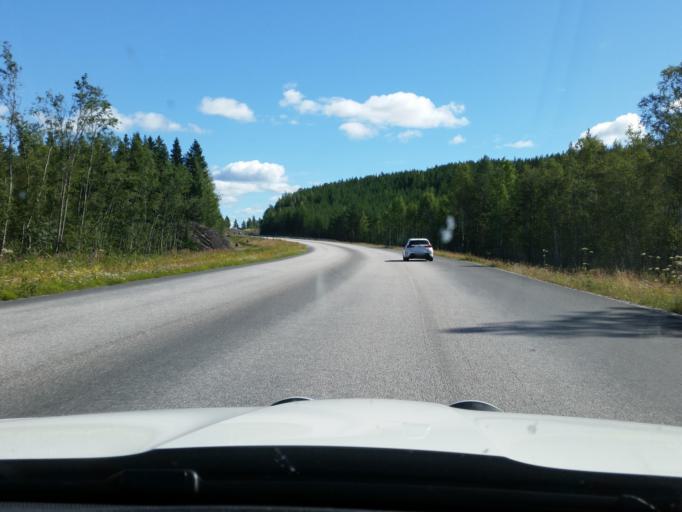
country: SE
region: Norrbotten
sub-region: Pitea Kommun
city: Bergsviken
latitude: 65.3150
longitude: 21.3506
